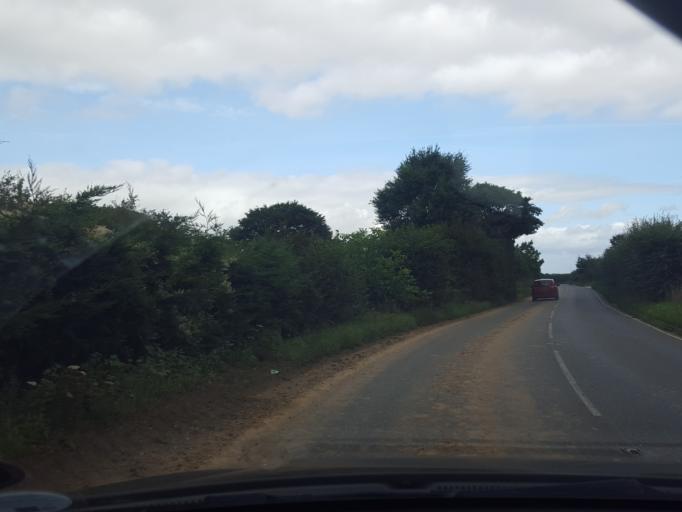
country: GB
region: England
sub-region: Essex
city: Great Bentley
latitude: 51.8624
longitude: 1.0353
